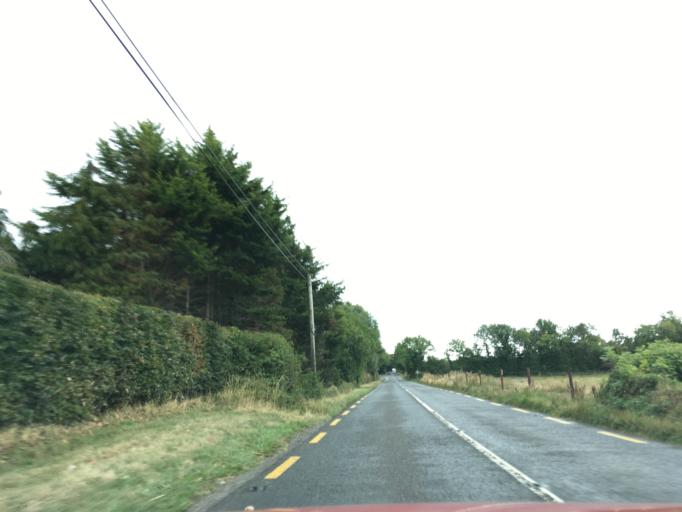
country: IE
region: Munster
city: Fethard
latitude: 52.4306
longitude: -7.7801
